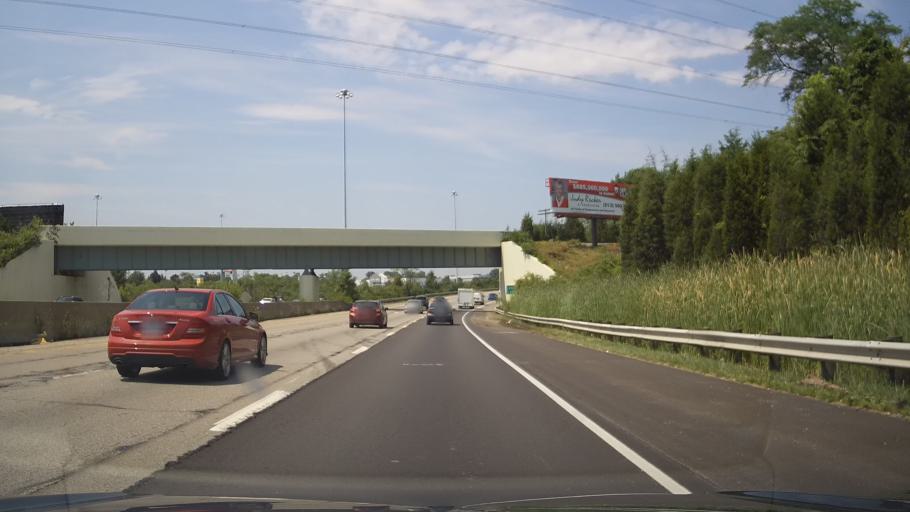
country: US
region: Ohio
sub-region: Hamilton County
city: Golf Manor
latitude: 39.1670
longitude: -84.4244
